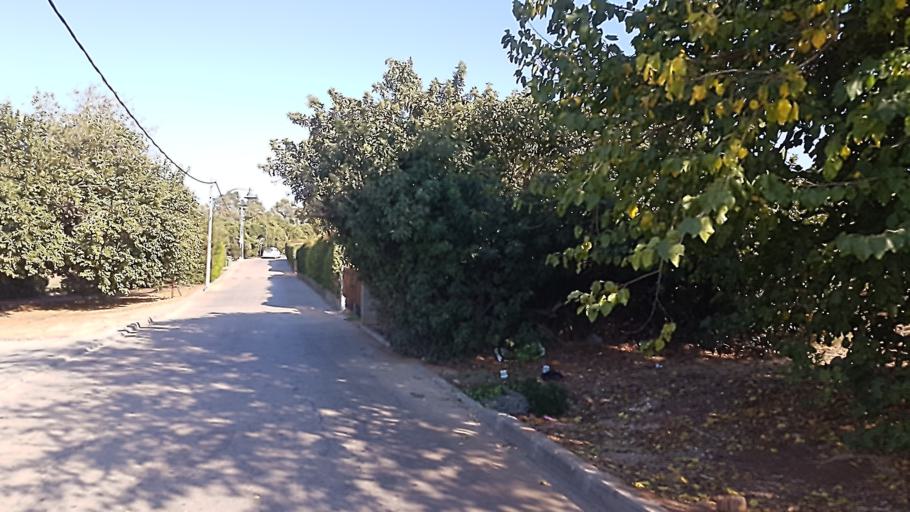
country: IL
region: Central District
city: Kfar Saba
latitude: 32.2034
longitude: 34.9122
